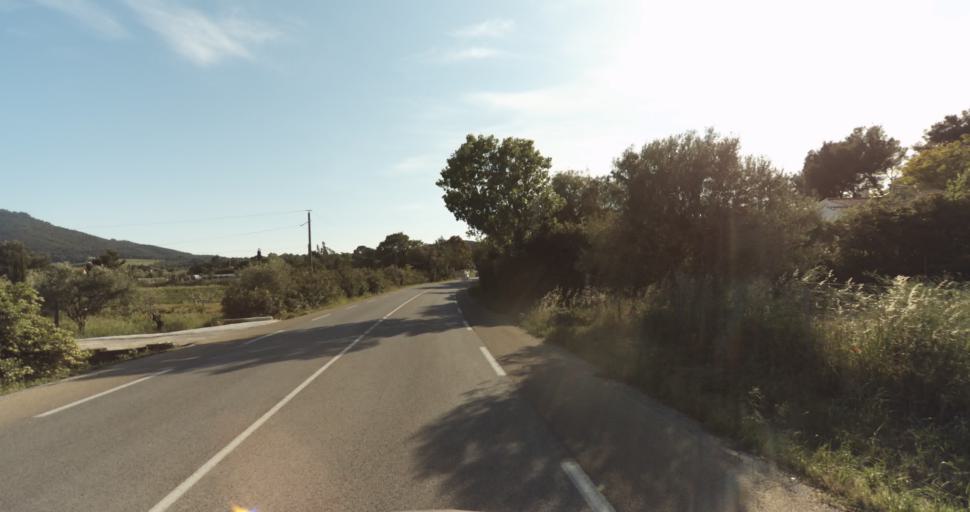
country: FR
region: Provence-Alpes-Cote d'Azur
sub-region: Departement du Var
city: Carqueiranne
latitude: 43.1121
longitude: 6.0529
